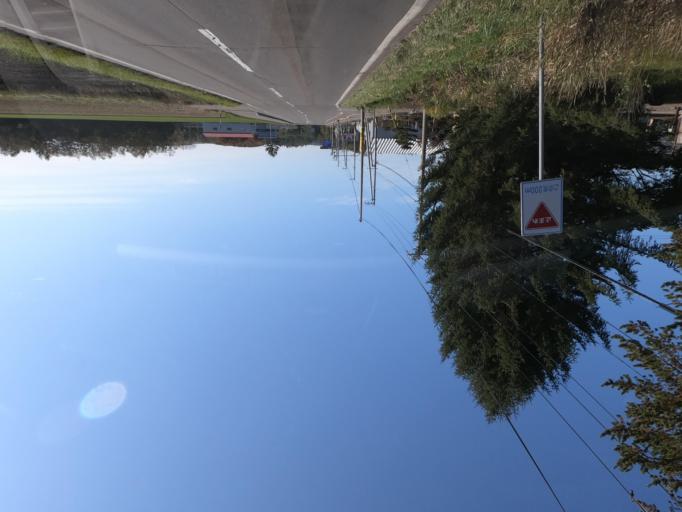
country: JP
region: Hokkaido
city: Otofuke
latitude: 42.9603
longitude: 143.2477
